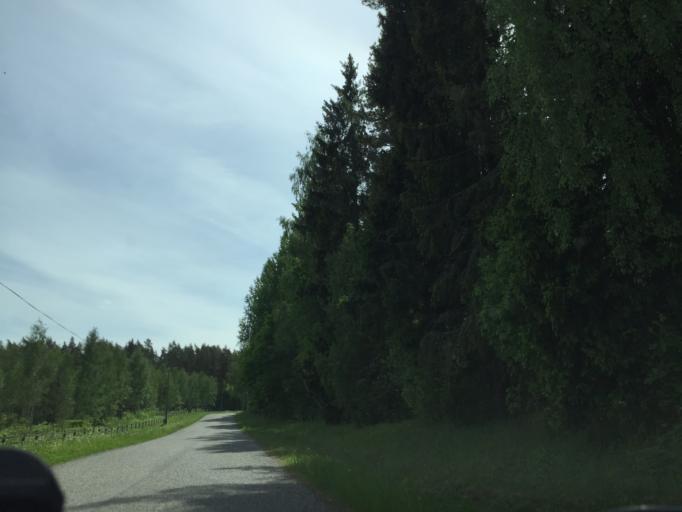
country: LV
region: Koceni
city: Koceni
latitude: 57.4927
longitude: 25.3635
